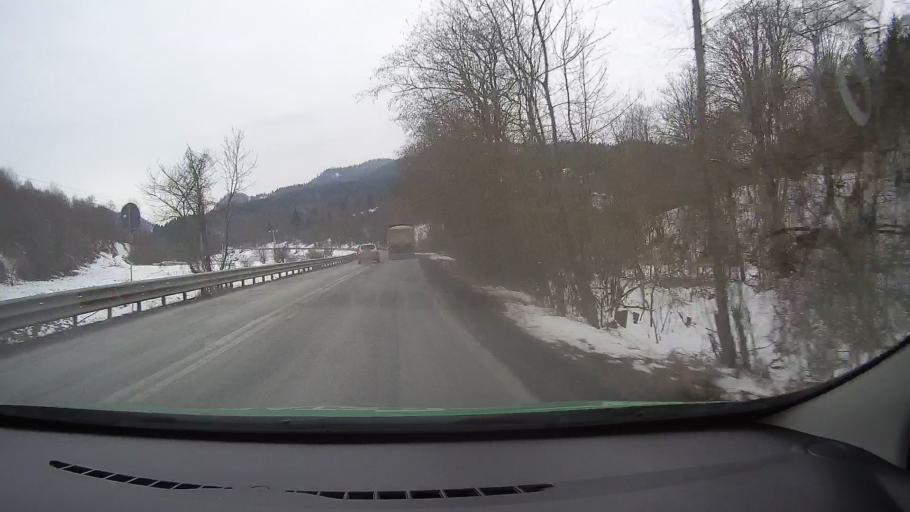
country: RO
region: Brasov
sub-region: Oras Rasnov
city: Rasnov
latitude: 45.5296
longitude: 25.4992
